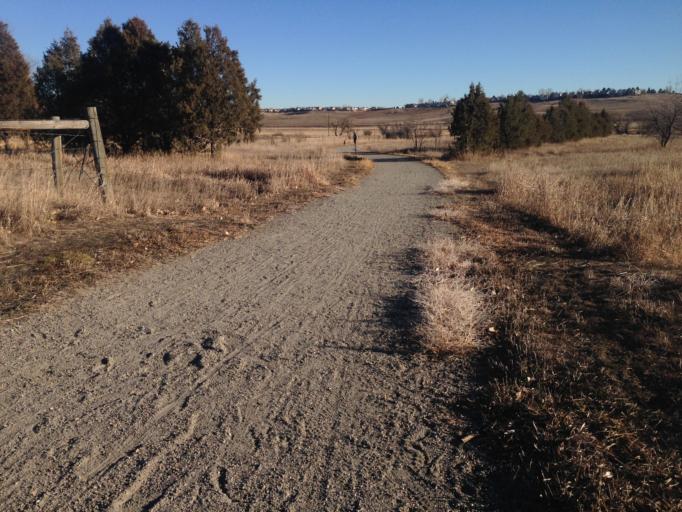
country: US
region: Colorado
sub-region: Broomfield County
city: Broomfield
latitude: 39.9444
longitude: -105.1044
